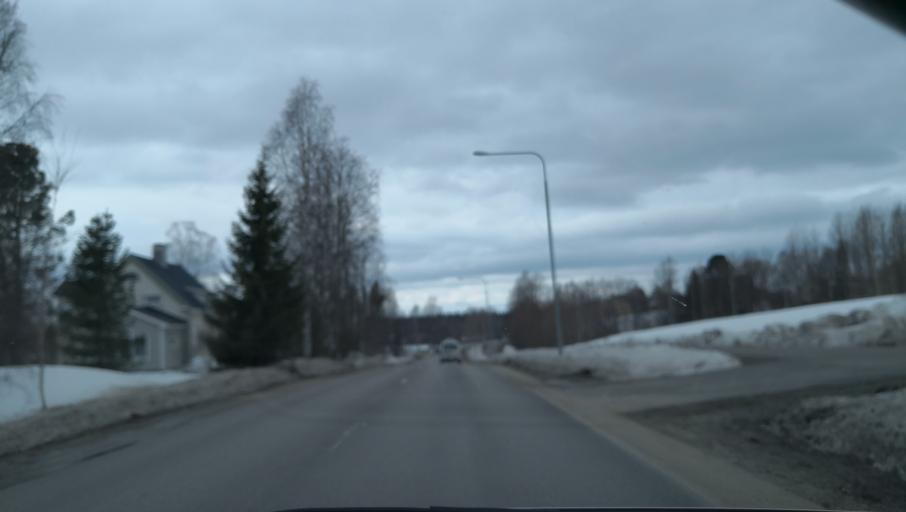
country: SE
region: Vaesterbotten
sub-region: Vannas Kommun
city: Vaennaes
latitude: 63.9173
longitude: 19.7934
